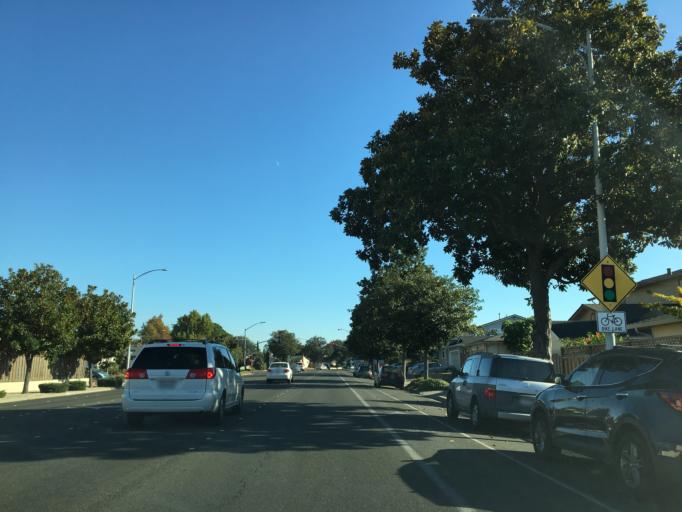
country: US
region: California
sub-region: Santa Clara County
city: Milpitas
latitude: 37.4243
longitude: -121.8786
